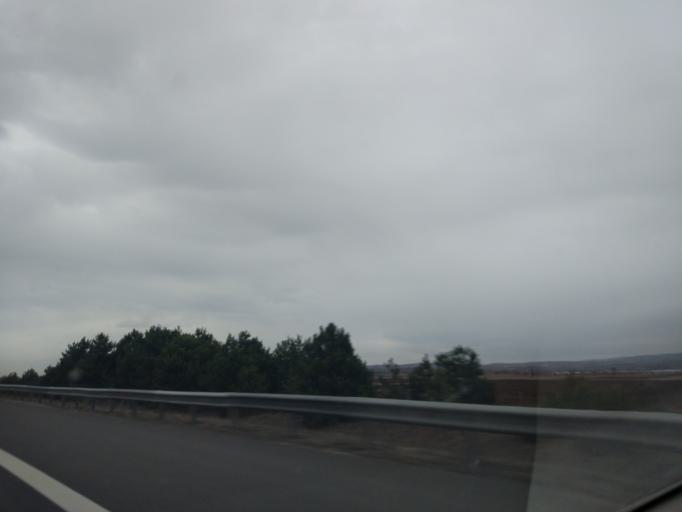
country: TR
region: Bolu
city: Gerede
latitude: 40.7403
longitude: 32.1705
